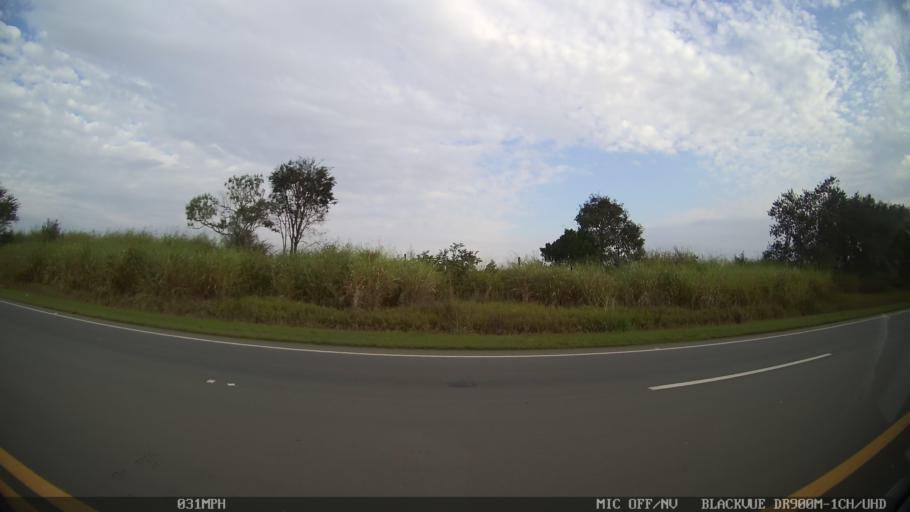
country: BR
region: Sao Paulo
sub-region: Cosmopolis
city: Cosmopolis
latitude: -22.6279
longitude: -47.2713
